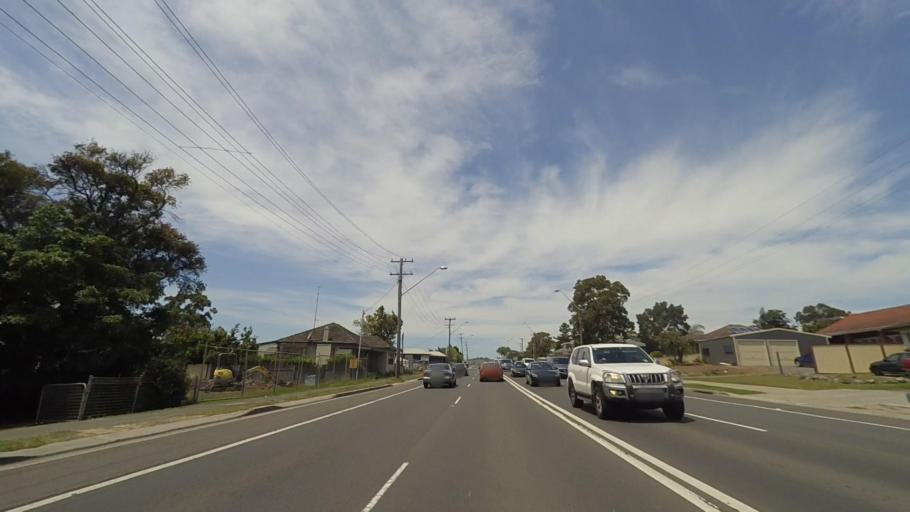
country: AU
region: New South Wales
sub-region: Shellharbour
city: Albion Park Rail
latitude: -34.5645
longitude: 150.7991
